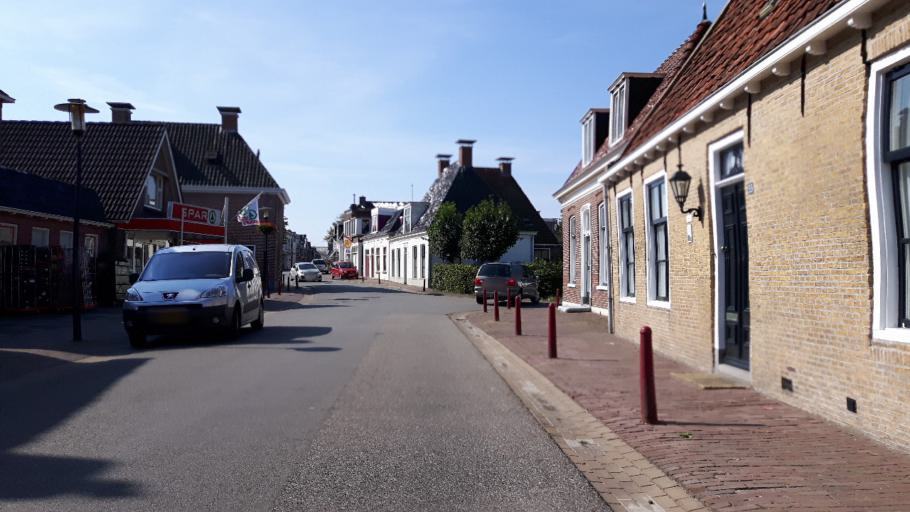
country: NL
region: Friesland
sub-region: Gemeente Ferwerderadiel
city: Ferwert
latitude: 53.3394
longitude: 5.8259
